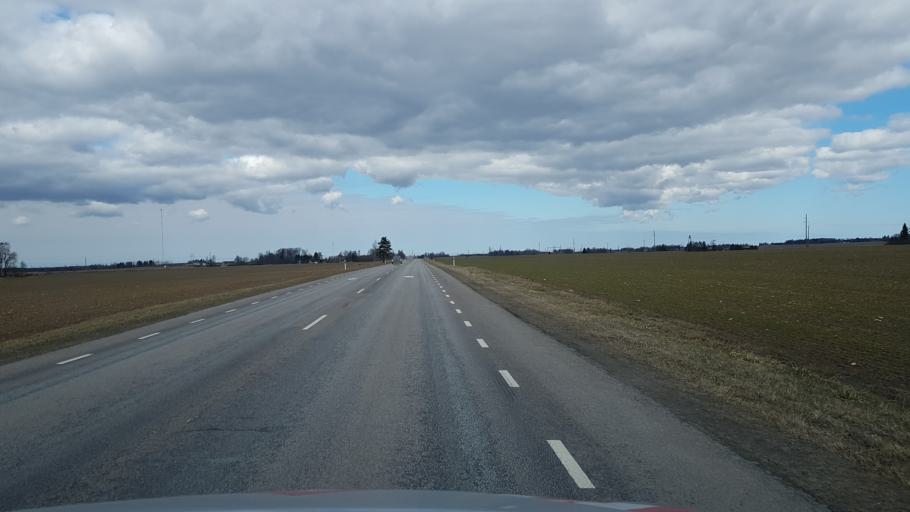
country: EE
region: Laeaene-Virumaa
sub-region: Vaeike-Maarja vald
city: Vaike-Maarja
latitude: 59.2002
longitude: 26.2680
